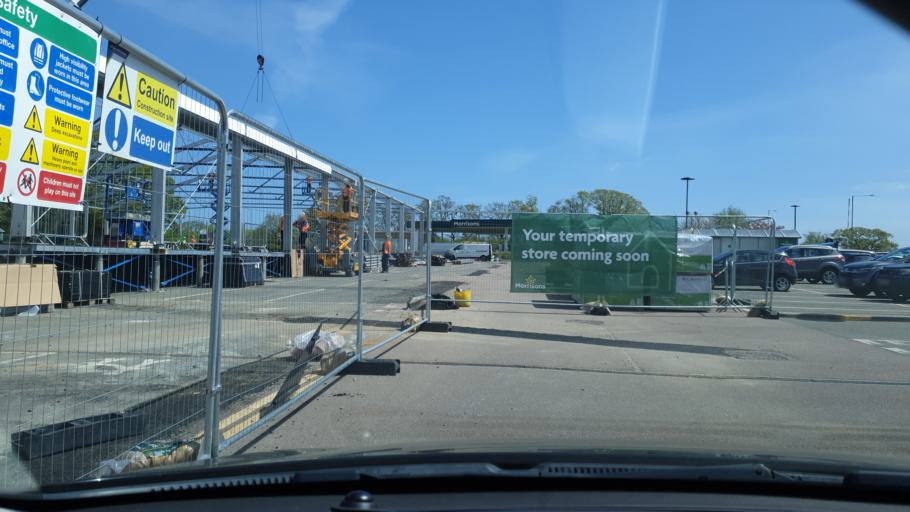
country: GB
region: England
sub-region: Essex
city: Little Clacton
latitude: 51.8202
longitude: 1.1499
